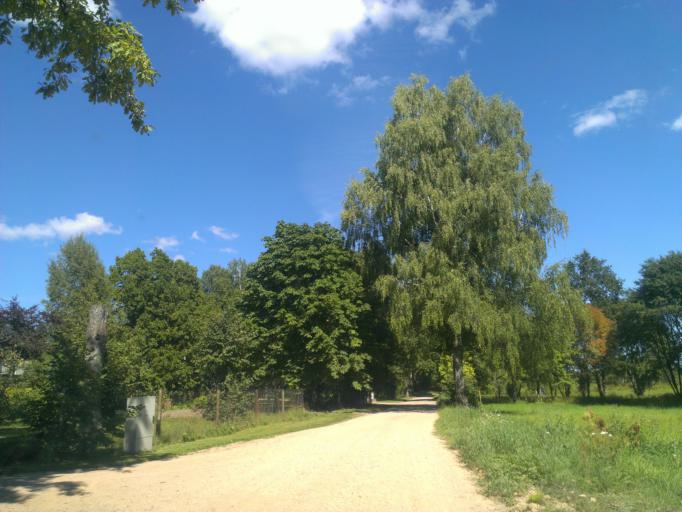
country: LV
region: Malpils
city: Malpils
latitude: 57.0094
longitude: 24.9680
